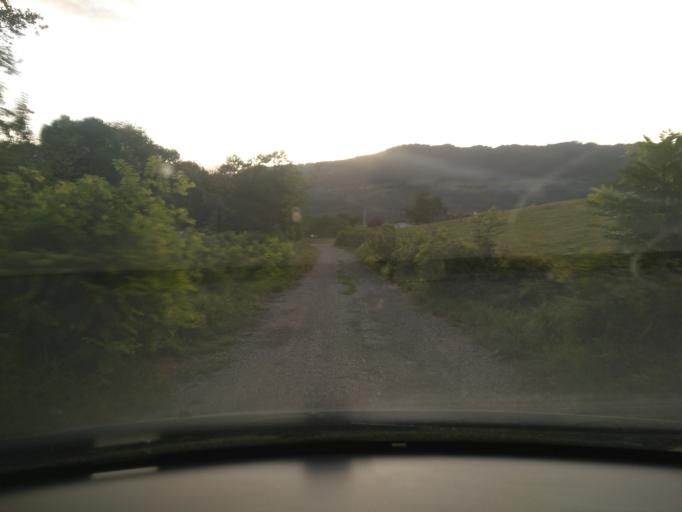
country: FR
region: Rhone-Alpes
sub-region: Departement de la Savoie
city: La Rochette
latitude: 45.4529
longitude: 6.1277
